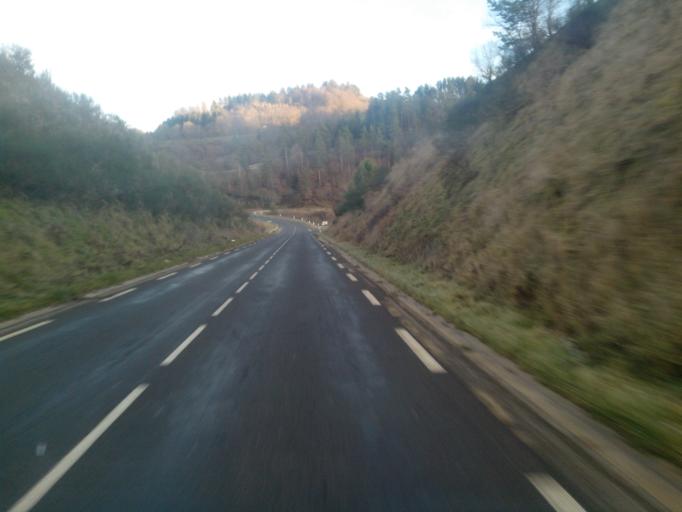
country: FR
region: Auvergne
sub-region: Departement du Cantal
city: Riom-es-Montagnes
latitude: 45.2486
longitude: 2.7073
